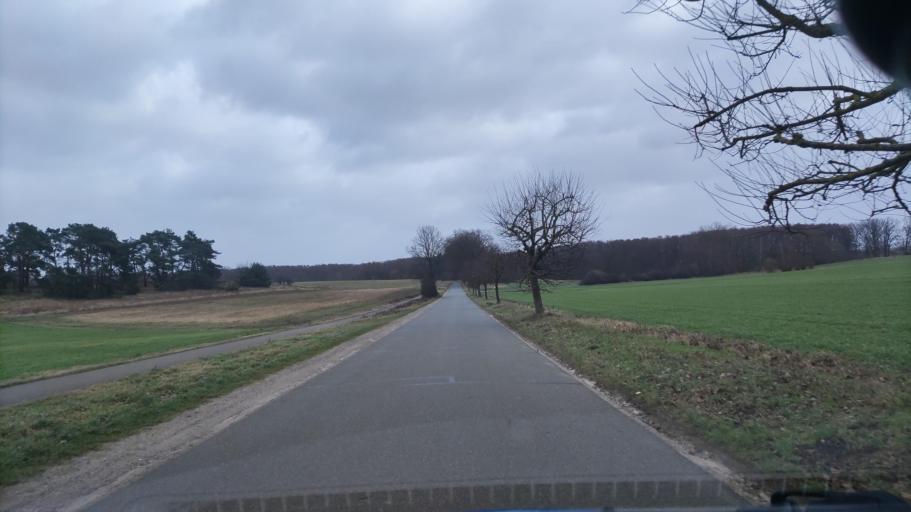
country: DE
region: Lower Saxony
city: Sudergellersen
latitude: 53.2073
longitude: 10.3126
